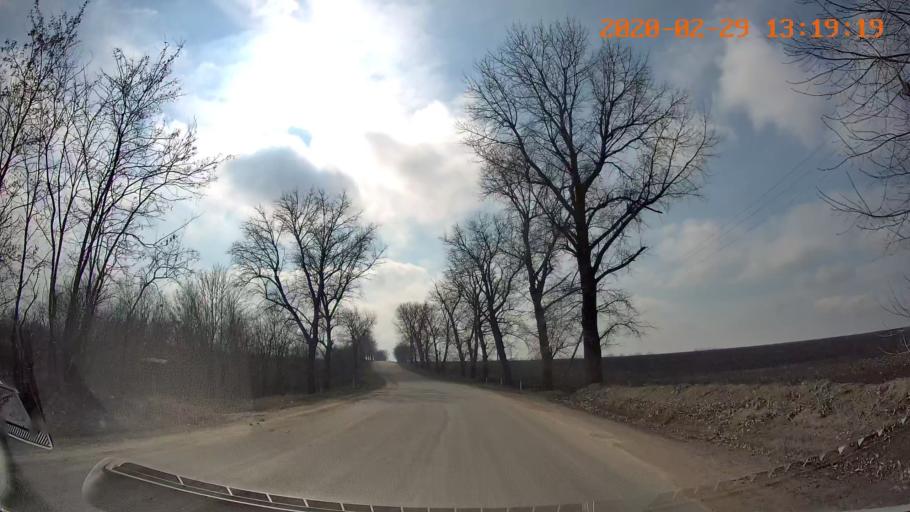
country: MD
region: Telenesti
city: Camenca
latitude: 47.9898
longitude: 28.6520
